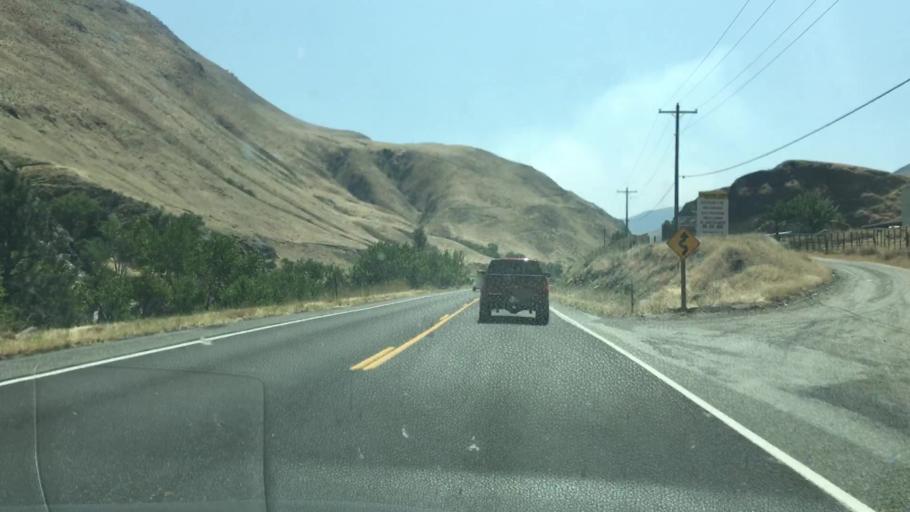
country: US
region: Idaho
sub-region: Valley County
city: McCall
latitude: 45.3826
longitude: -116.3511
